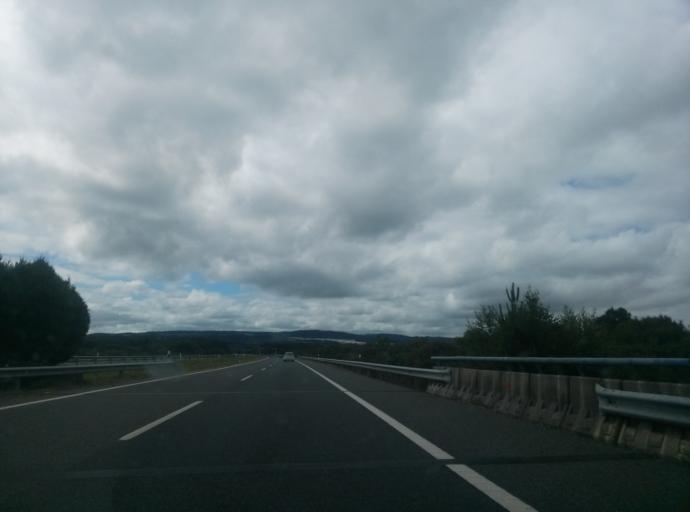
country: ES
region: Galicia
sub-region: Provincia de Lugo
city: Begonte
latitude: 43.1730
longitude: -7.7078
